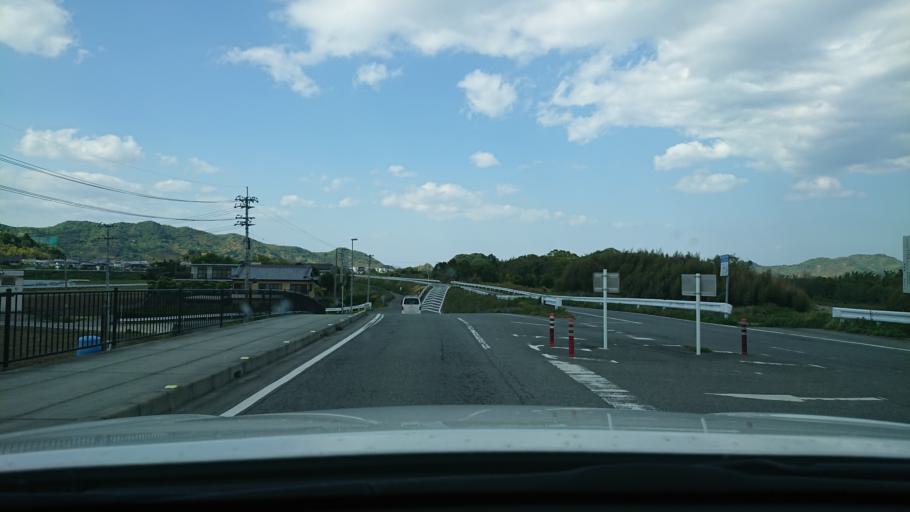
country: JP
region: Tokushima
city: Komatsushimacho
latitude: 33.9955
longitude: 134.5474
